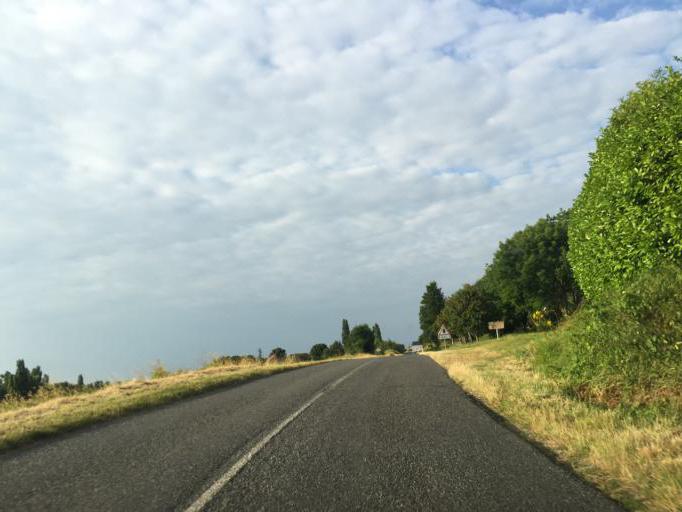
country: FR
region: Auvergne
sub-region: Departement de l'Allier
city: Saint-Remy-en-Rollat
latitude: 46.1769
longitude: 3.4155
